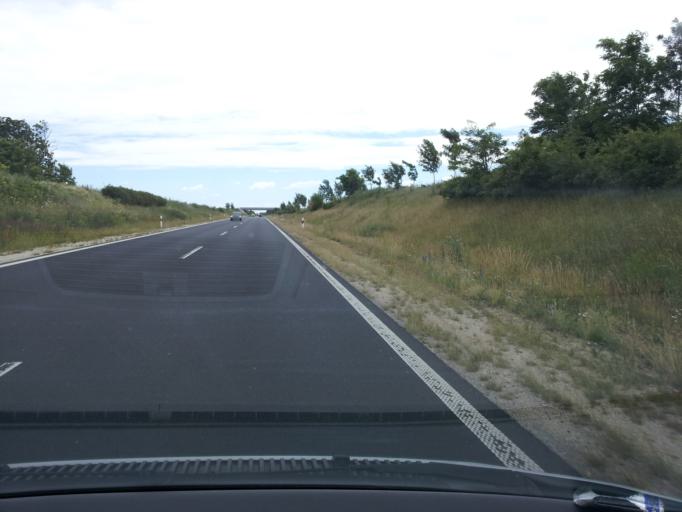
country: HU
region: Veszprem
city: Balatonkenese
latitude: 47.0631
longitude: 18.0951
